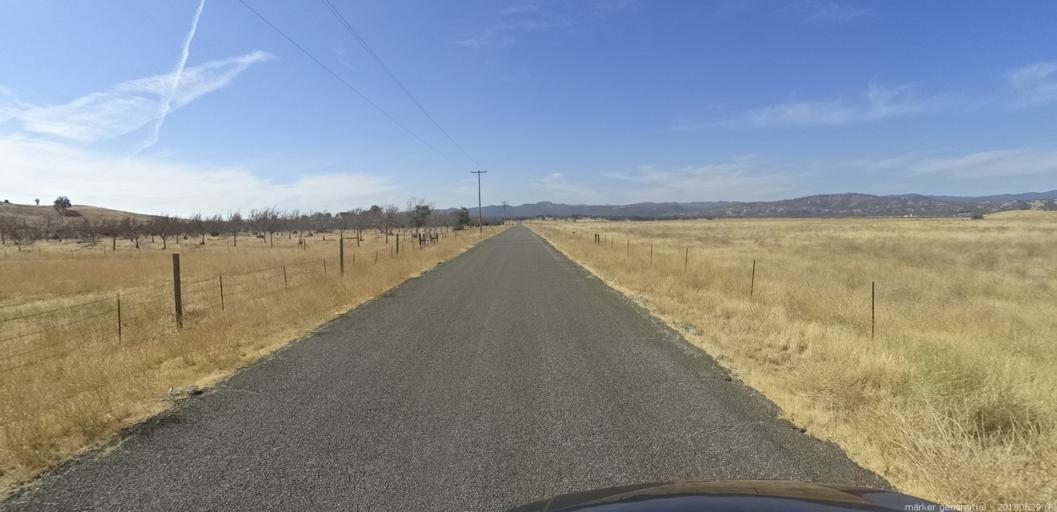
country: US
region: California
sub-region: Monterey County
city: King City
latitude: 35.9556
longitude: -121.1176
